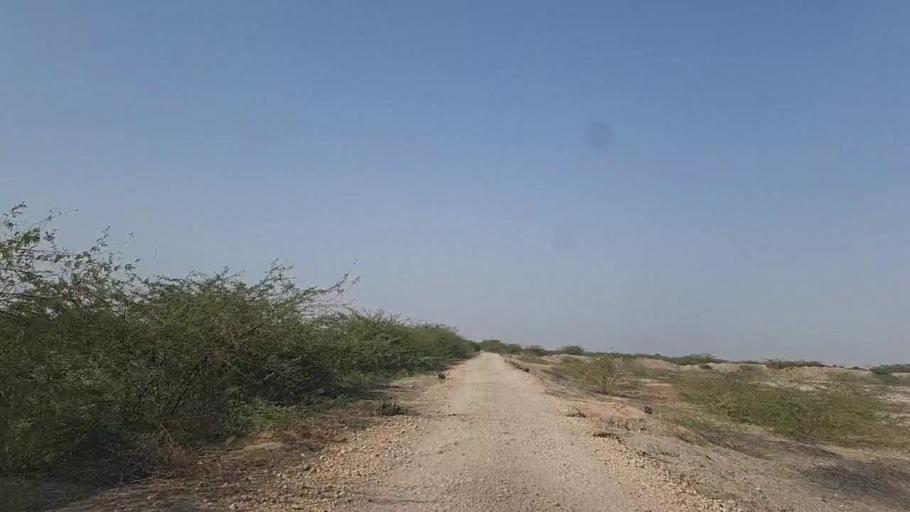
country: PK
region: Sindh
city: Naukot
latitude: 24.6083
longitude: 69.2747
